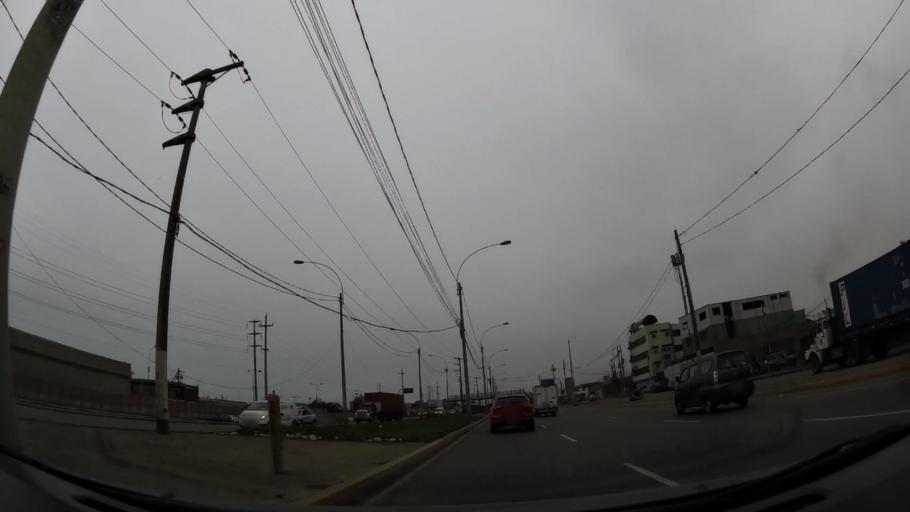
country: PE
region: Callao
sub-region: Callao
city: Callao
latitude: -11.9797
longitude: -77.1251
